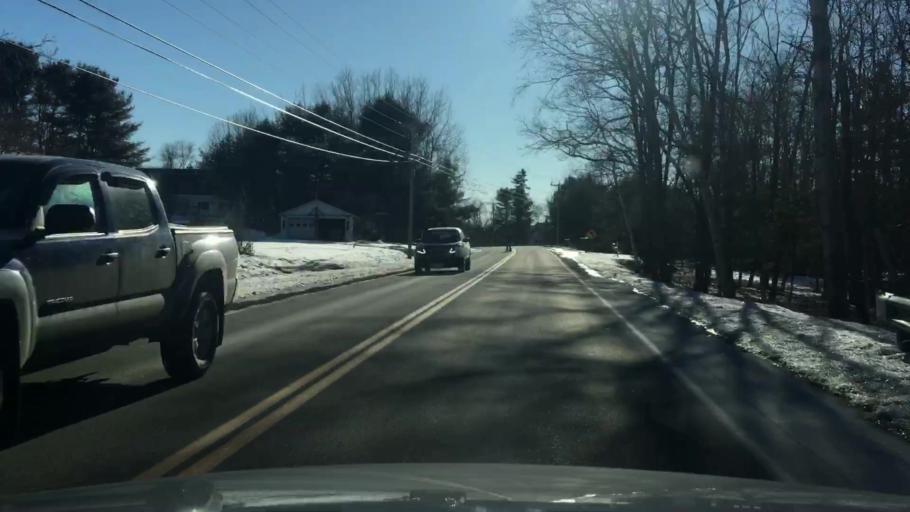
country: US
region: Maine
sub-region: Hancock County
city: Orland
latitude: 44.5439
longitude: -68.7443
